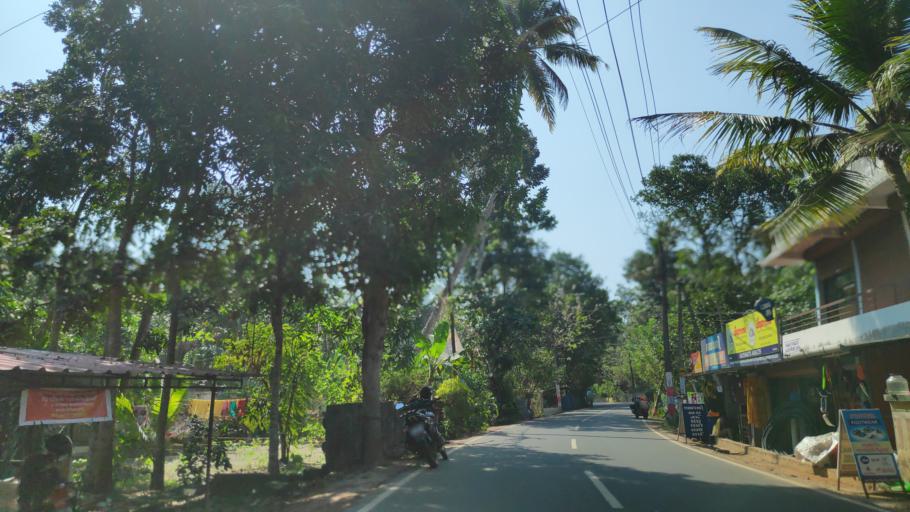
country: IN
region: Kerala
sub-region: Alappuzha
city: Shertallai
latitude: 9.6567
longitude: 76.3328
